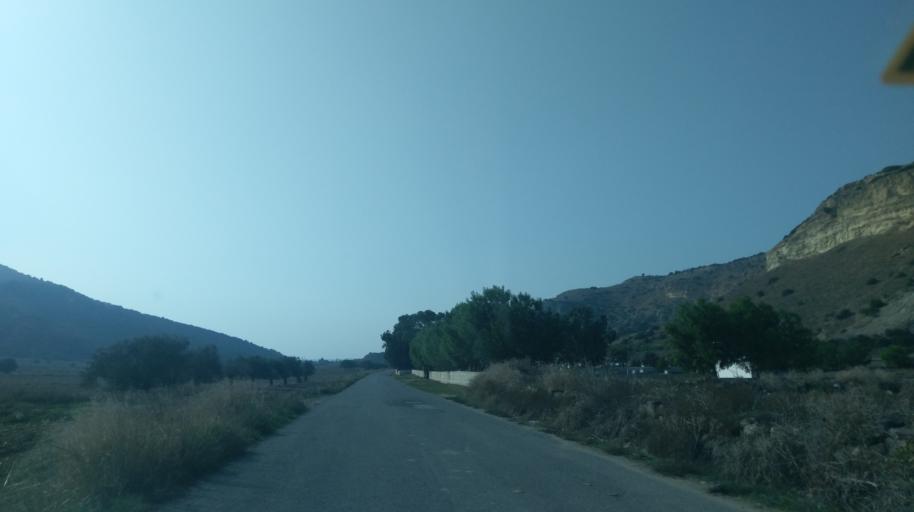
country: CY
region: Ammochostos
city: Rizokarpaso
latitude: 35.5156
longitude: 34.3013
